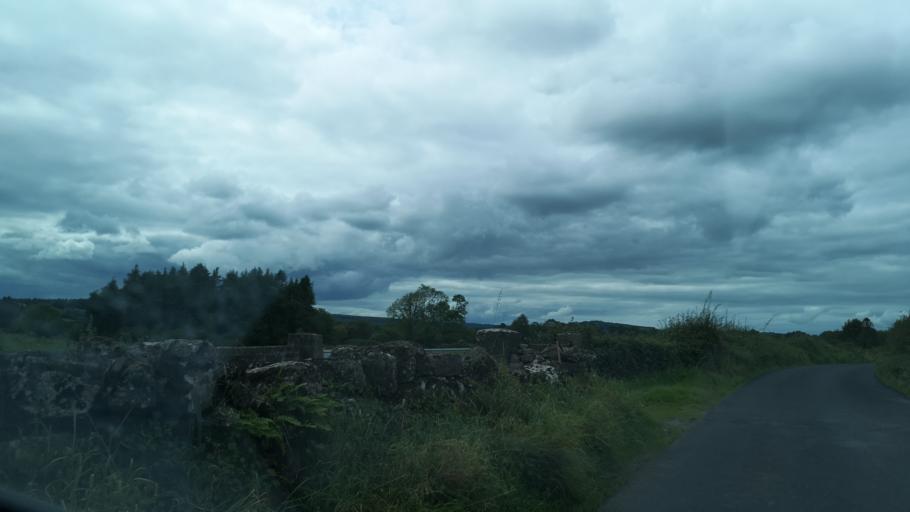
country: IE
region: Connaught
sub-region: County Galway
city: Loughrea
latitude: 53.1562
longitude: -8.4483
